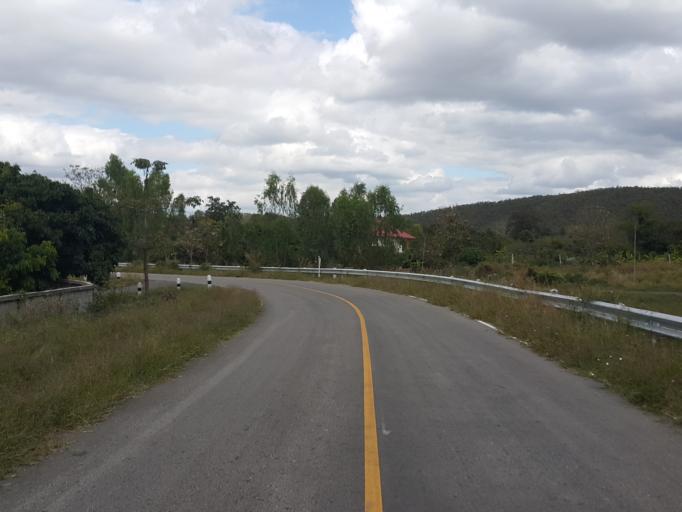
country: TH
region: Chiang Mai
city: San Kamphaeng
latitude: 18.8376
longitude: 99.1583
